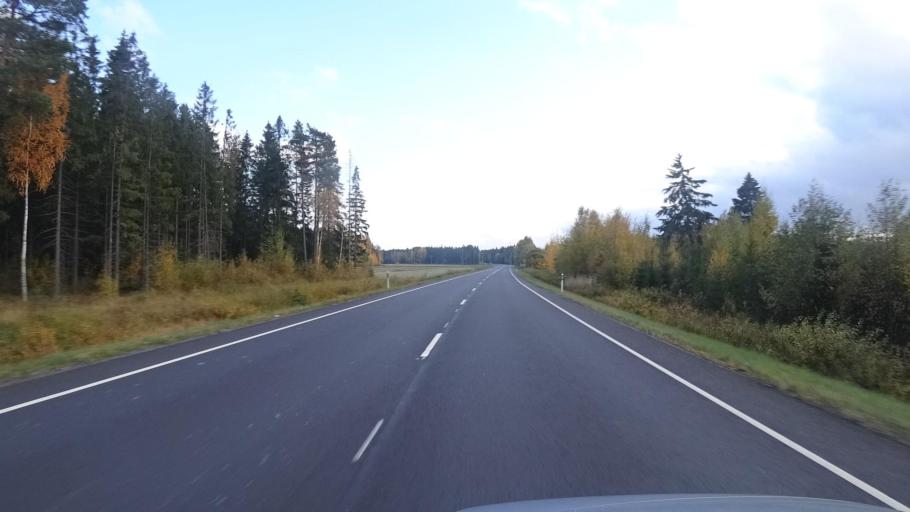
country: FI
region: Satakunta
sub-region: Rauma
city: Koeylioe
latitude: 61.0998
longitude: 22.2357
